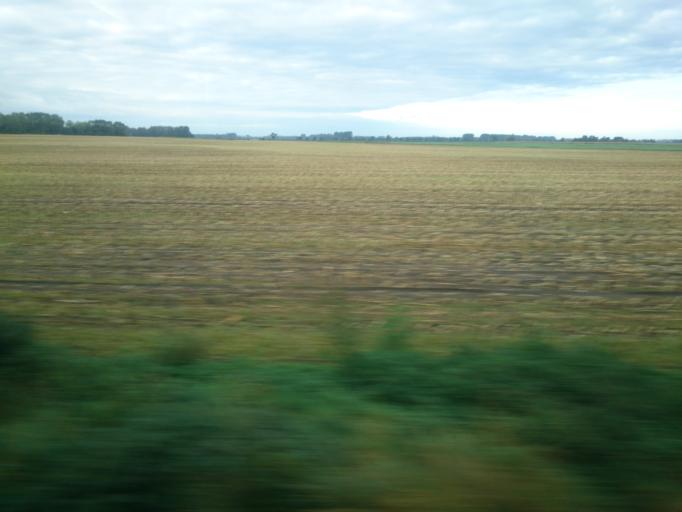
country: DE
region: Mecklenburg-Vorpommern
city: Ferdinandshof
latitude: 53.6733
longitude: 13.8862
